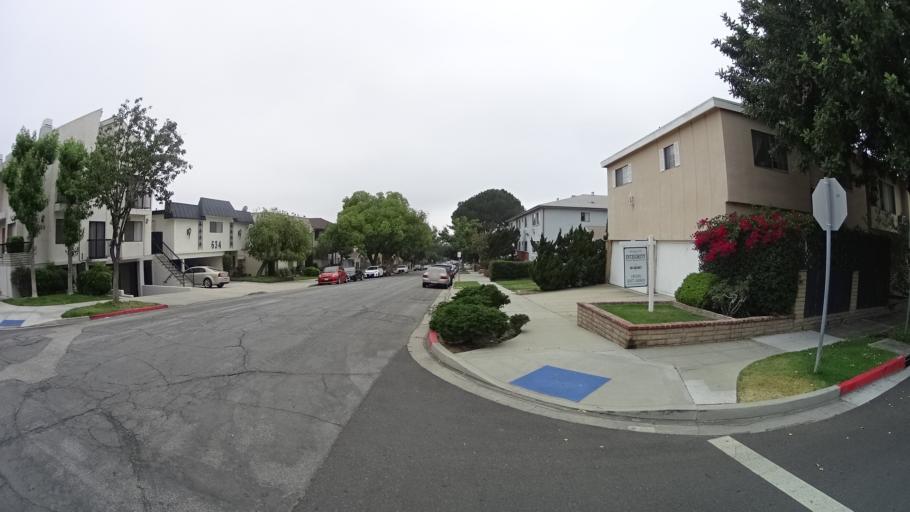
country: US
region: California
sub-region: Los Angeles County
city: Burbank
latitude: 34.1852
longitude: -118.3007
